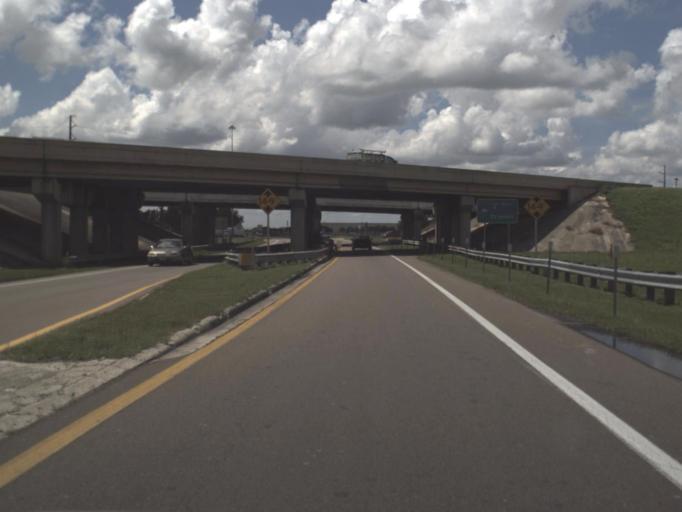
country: US
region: Florida
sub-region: Polk County
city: Gibsonia
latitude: 28.1410
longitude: -81.8981
